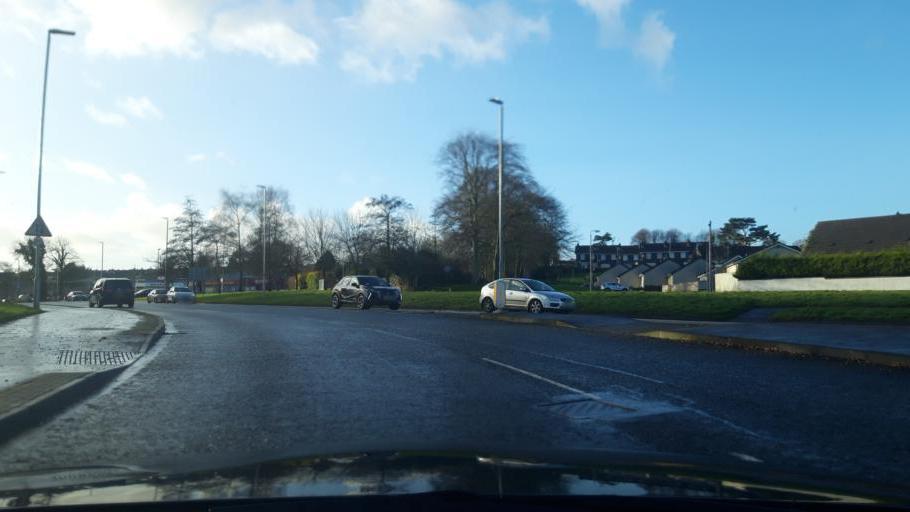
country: GB
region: Northern Ireland
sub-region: Coleraine District
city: Coleraine
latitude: 55.1202
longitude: -6.6796
